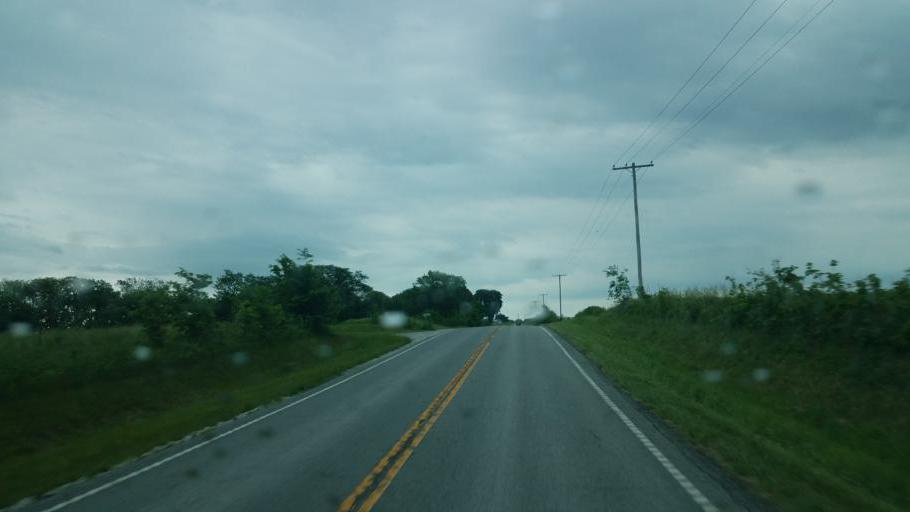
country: US
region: Missouri
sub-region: Cooper County
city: Boonville
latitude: 38.8281
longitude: -92.6099
